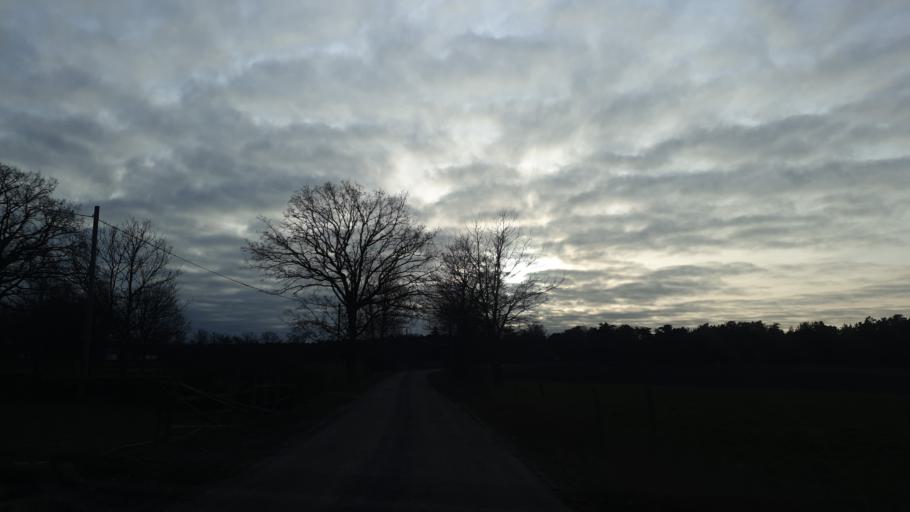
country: SE
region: Kalmar
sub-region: Torsas Kommun
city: Torsas
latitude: 56.3043
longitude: 16.0385
